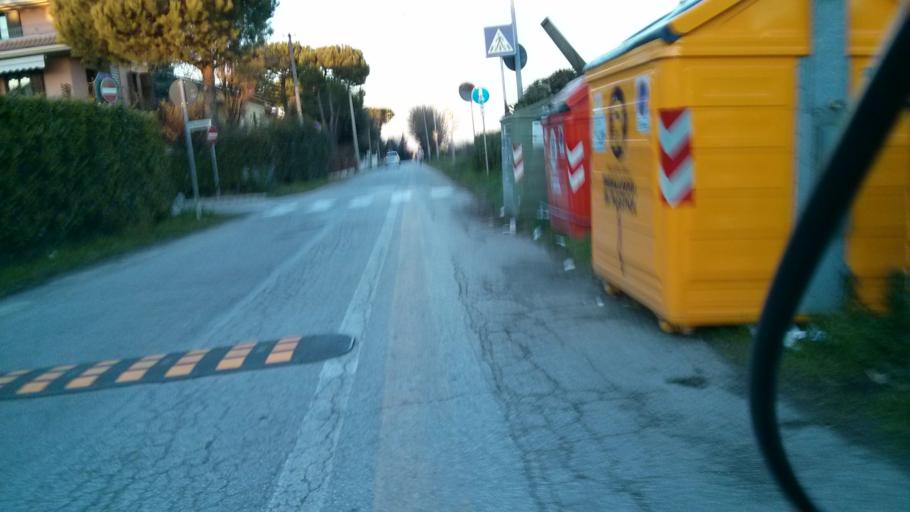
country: IT
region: The Marches
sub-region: Provincia di Pesaro e Urbino
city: Fano
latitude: 43.8444
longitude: 13.0063
